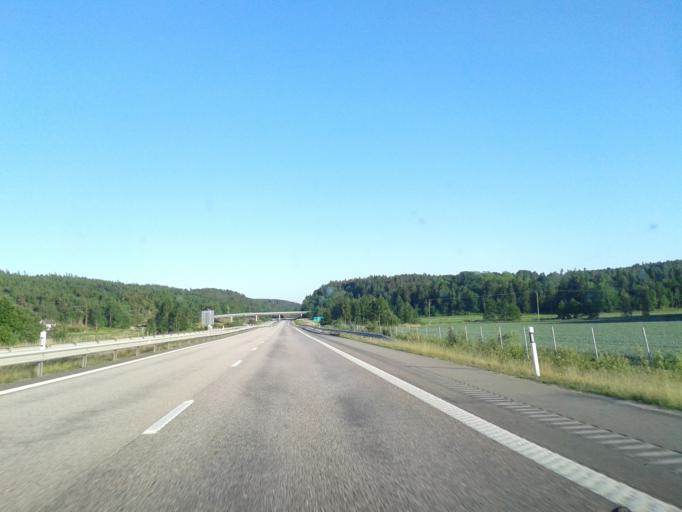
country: SE
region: Vaestra Goetaland
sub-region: Uddevalla Kommun
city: Ljungskile
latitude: 58.2804
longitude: 11.8817
